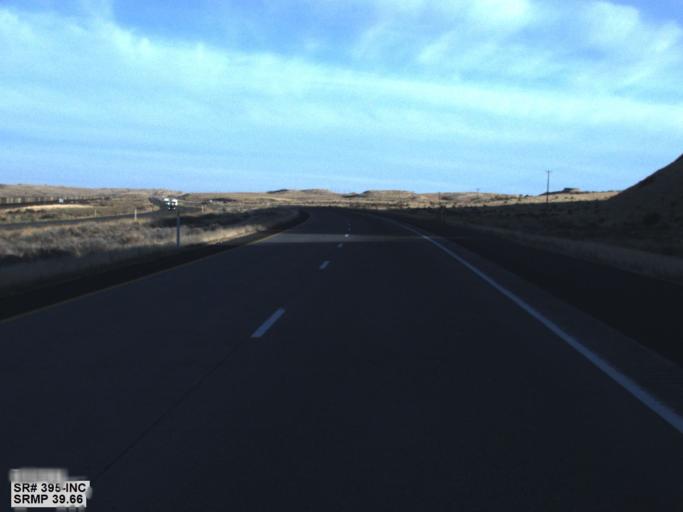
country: US
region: Washington
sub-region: Franklin County
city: Basin City
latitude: 46.4810
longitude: -119.0104
